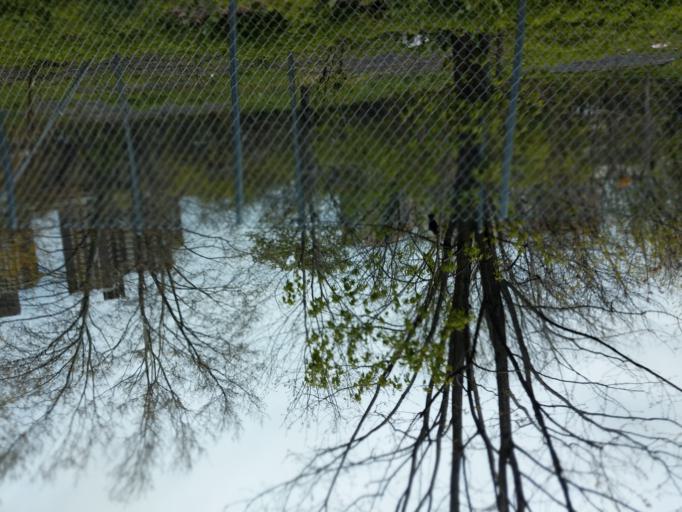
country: US
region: New York
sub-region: Bronx
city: The Bronx
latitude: 40.8395
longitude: -73.8780
